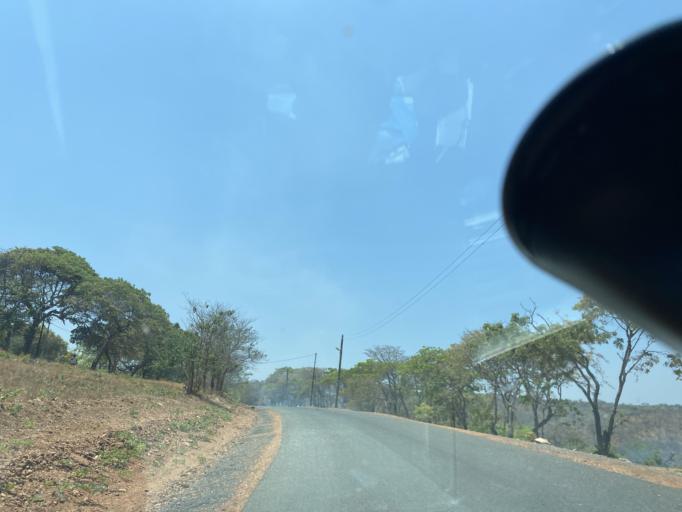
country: ZM
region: Lusaka
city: Kafue
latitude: -15.8662
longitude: 28.4451
